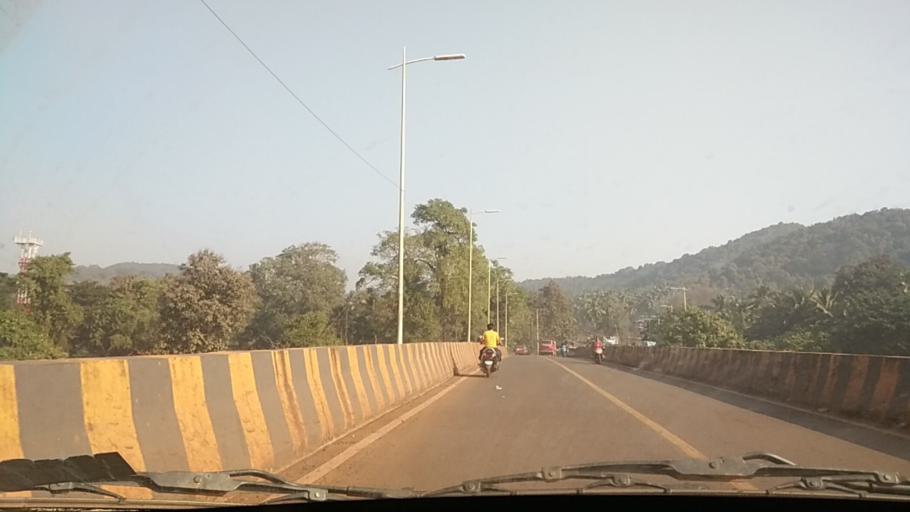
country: IN
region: Goa
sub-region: South Goa
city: Curchorem
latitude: 15.2664
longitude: 74.1114
